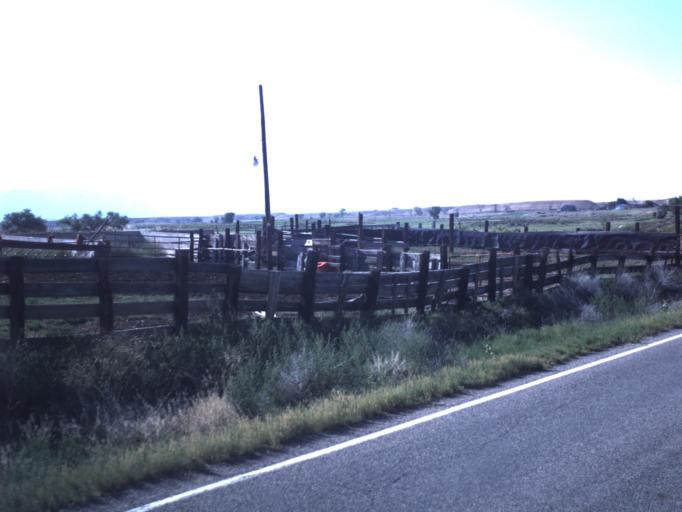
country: US
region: Utah
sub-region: Emery County
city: Huntington
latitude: 39.3582
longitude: -110.8521
